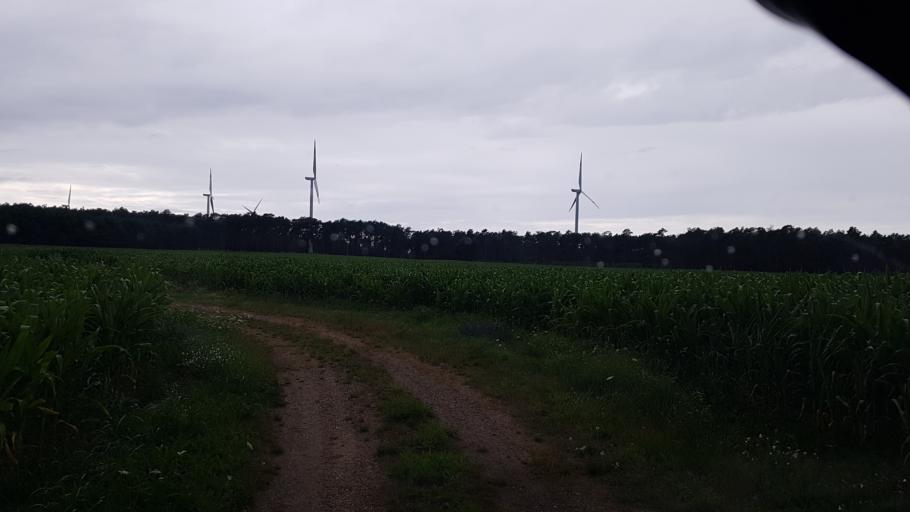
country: DE
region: Brandenburg
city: Schlieben
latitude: 51.6679
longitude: 13.3703
